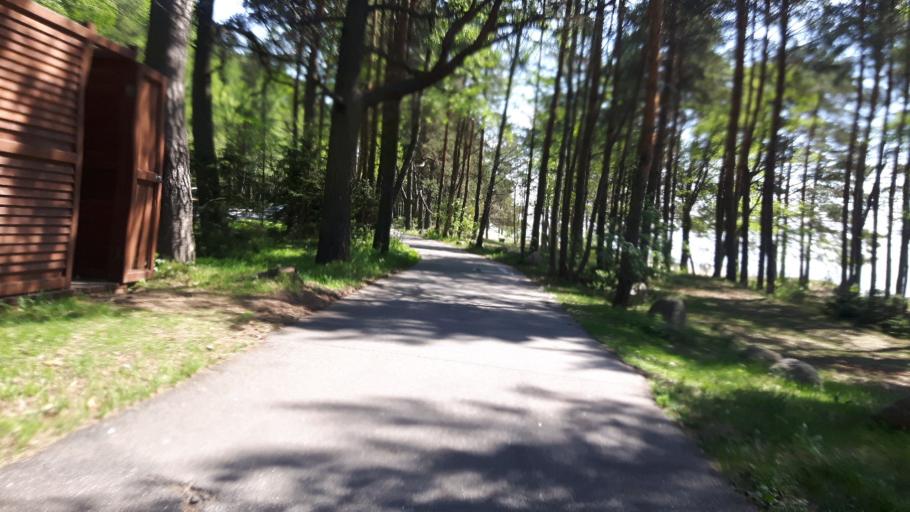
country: RU
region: St.-Petersburg
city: Komarovo
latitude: 60.1793
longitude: 29.7800
